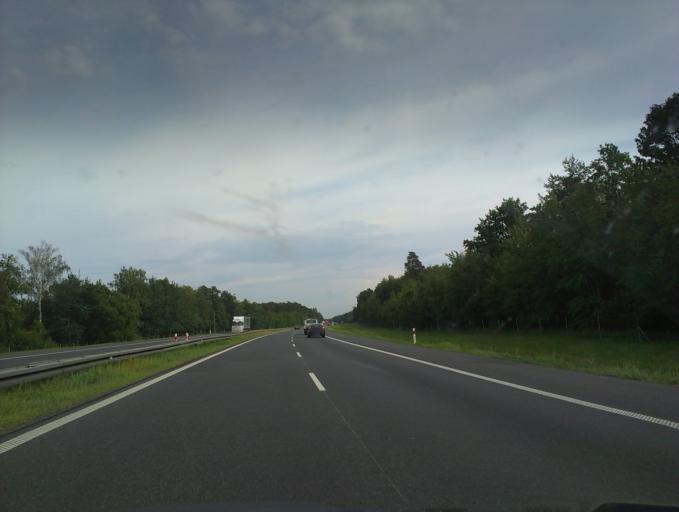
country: PL
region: Opole Voivodeship
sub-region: Powiat brzeski
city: Lewin Brzeski
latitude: 50.7045
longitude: 17.6145
